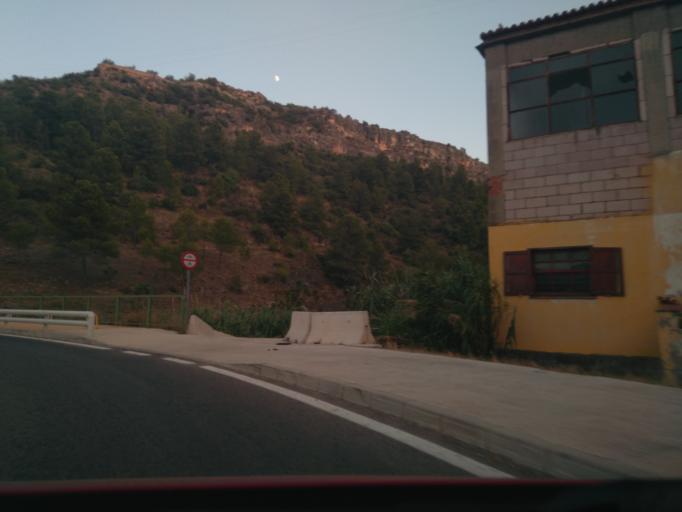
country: ES
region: Valencia
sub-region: Provincia de Valencia
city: Sumacarcer
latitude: 39.0904
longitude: -0.6297
